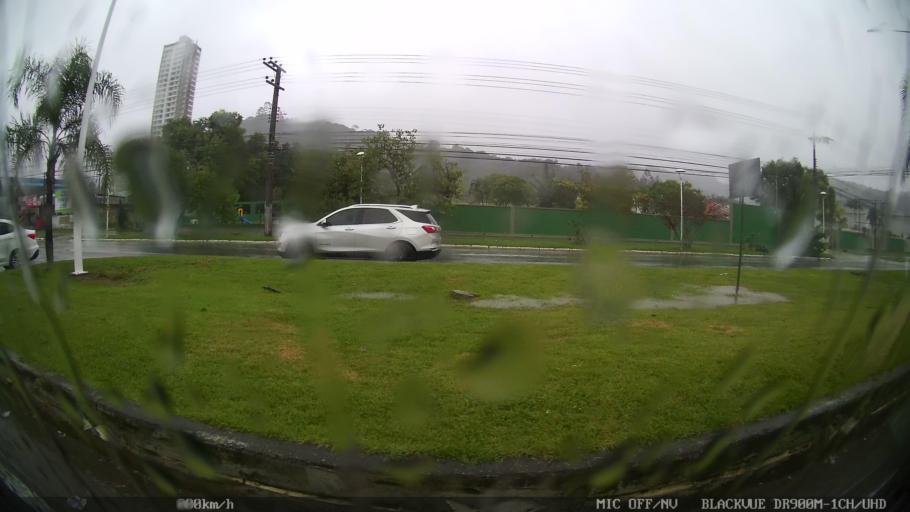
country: BR
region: Santa Catarina
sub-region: Balneario Camboriu
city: Balneario Camboriu
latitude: -26.9472
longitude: -48.6404
